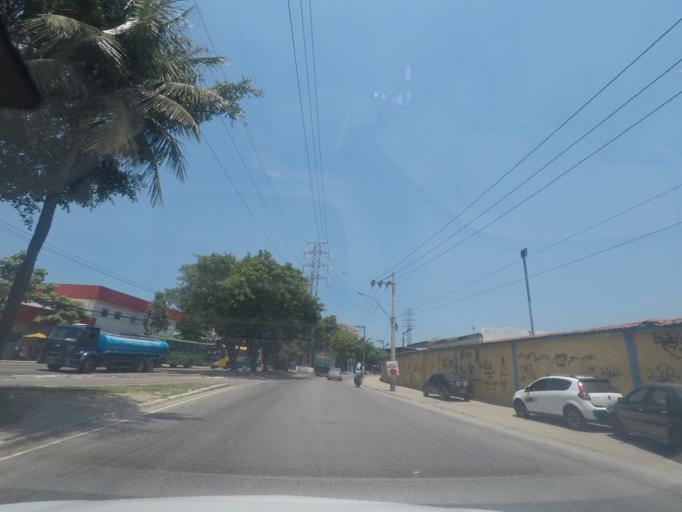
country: BR
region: Rio de Janeiro
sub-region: Duque De Caxias
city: Duque de Caxias
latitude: -22.7941
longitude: -43.3068
